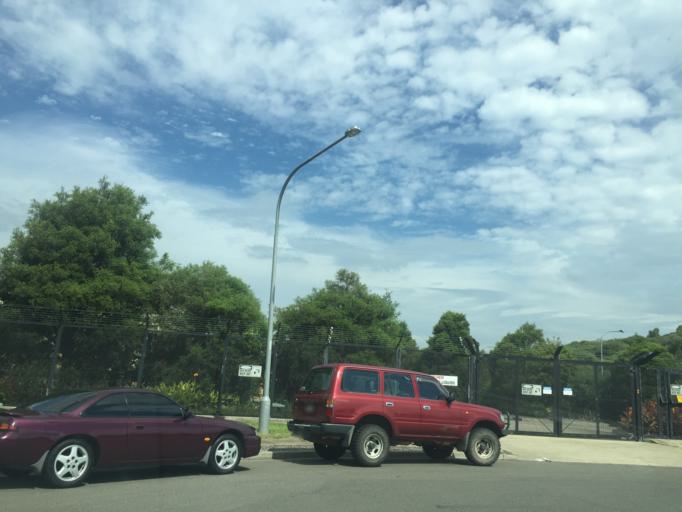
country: AU
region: New South Wales
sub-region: Holroyd
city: Girraween
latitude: -33.8163
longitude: 150.9179
